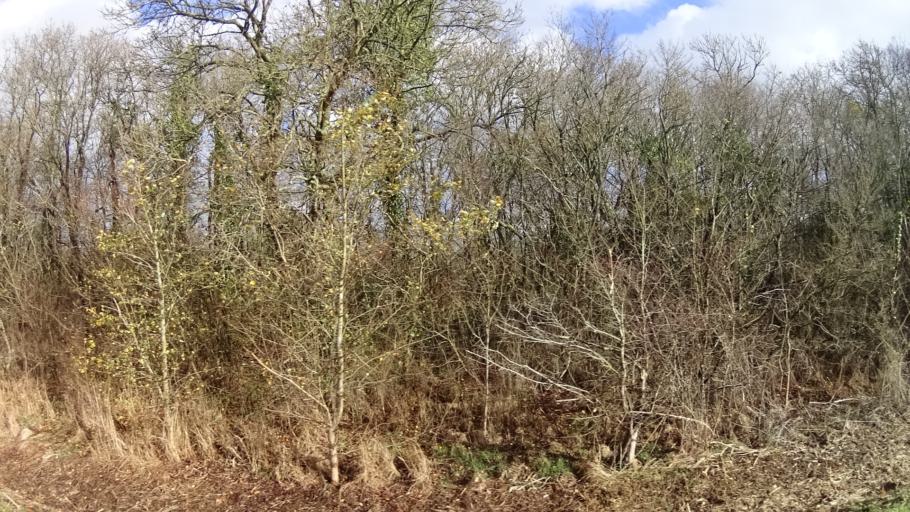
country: FR
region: Brittany
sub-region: Departement du Morbihan
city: Rieux
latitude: 47.5846
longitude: -2.0823
